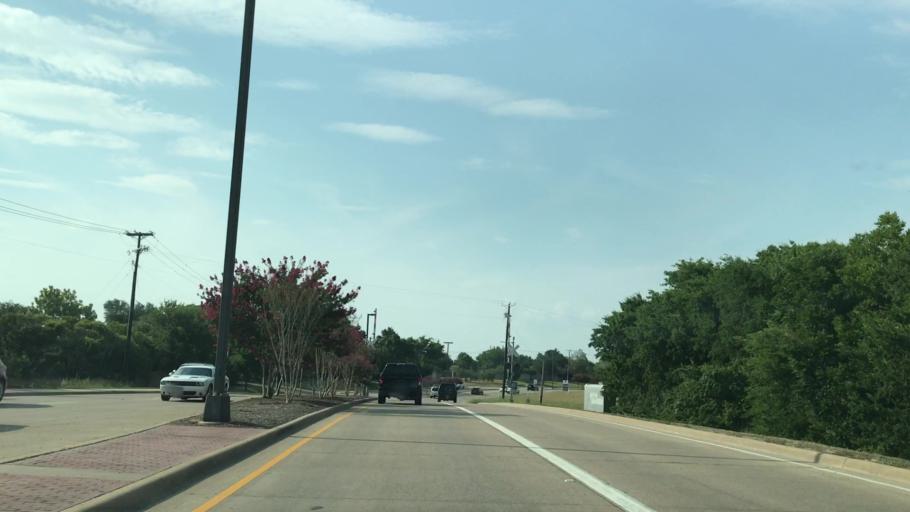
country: US
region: Texas
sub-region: Rockwall County
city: Rockwall
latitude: 32.9059
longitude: -96.4634
